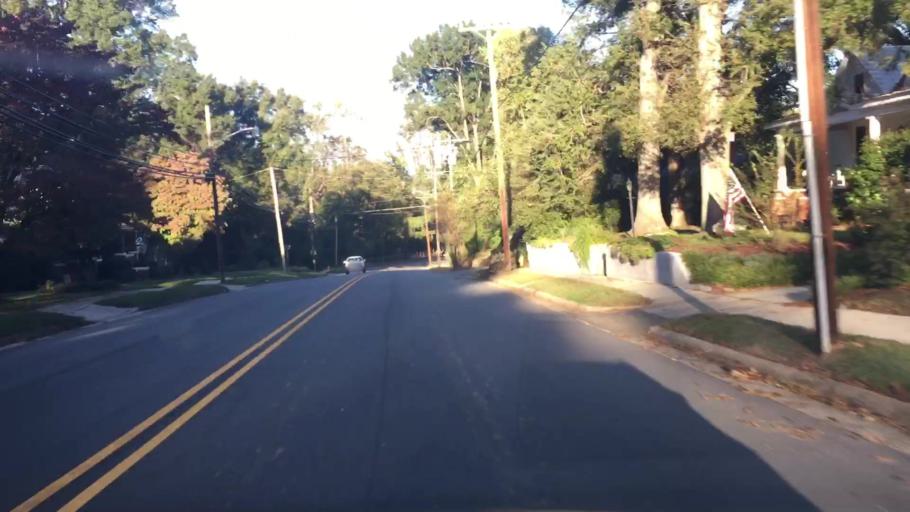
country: US
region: North Carolina
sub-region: Iredell County
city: Mooresville
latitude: 35.5797
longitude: -80.8080
